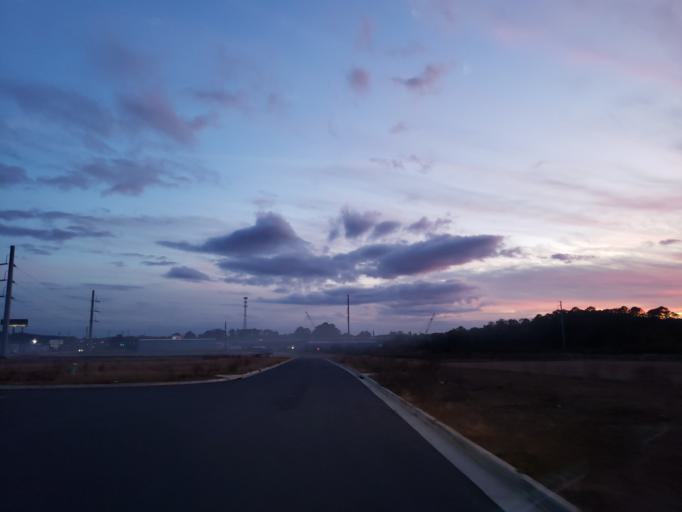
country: US
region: Georgia
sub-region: Bartow County
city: Cartersville
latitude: 34.2072
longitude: -84.8006
